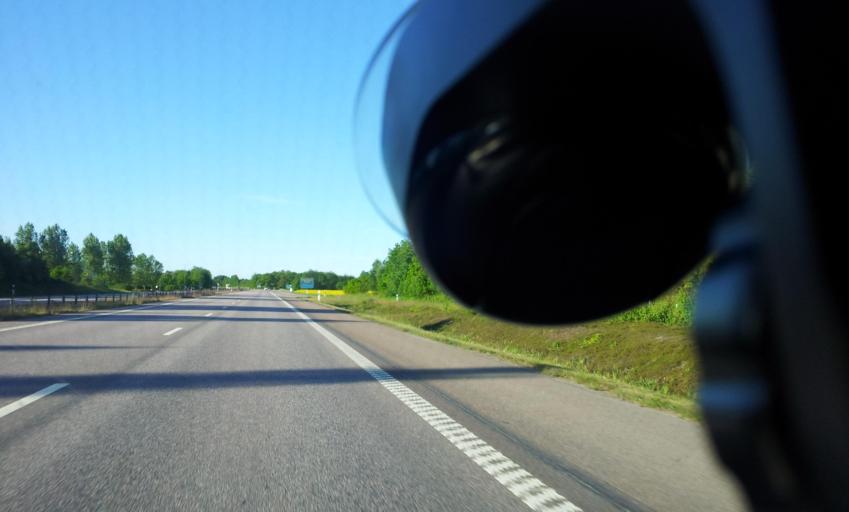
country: SE
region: Kalmar
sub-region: Kalmar Kommun
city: Lindsdal
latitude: 56.7116
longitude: 16.3140
